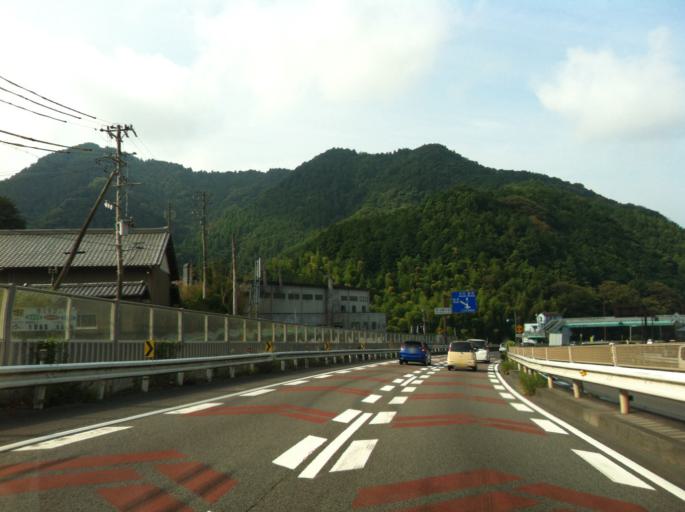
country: JP
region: Shizuoka
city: Yaizu
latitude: 34.9259
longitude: 138.3016
